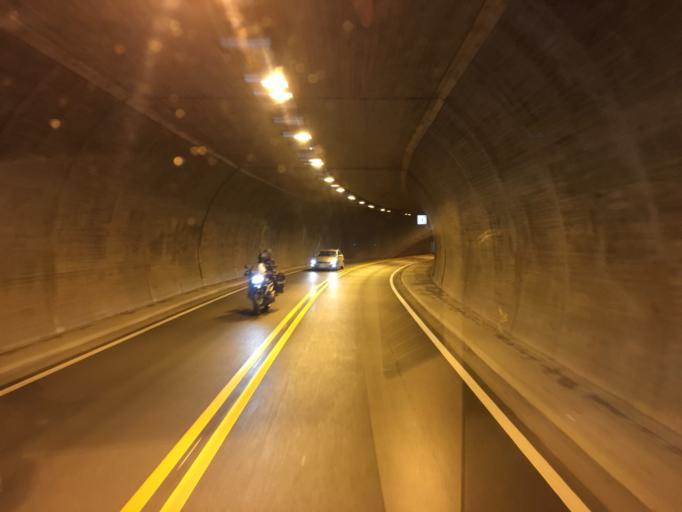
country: NO
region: Oppland
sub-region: Lillehammer
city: Lillehammer
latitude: 61.1151
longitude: 10.4569
